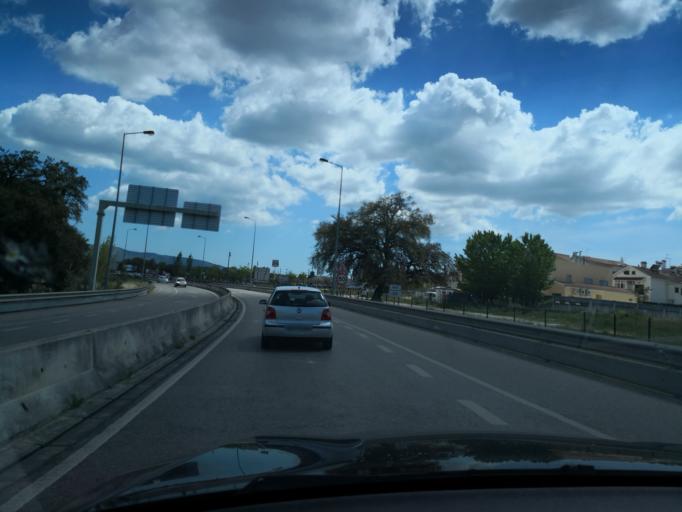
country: PT
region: Setubal
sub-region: Barreiro
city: Santo Antonio da Charneca
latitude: 38.5678
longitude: -9.0369
